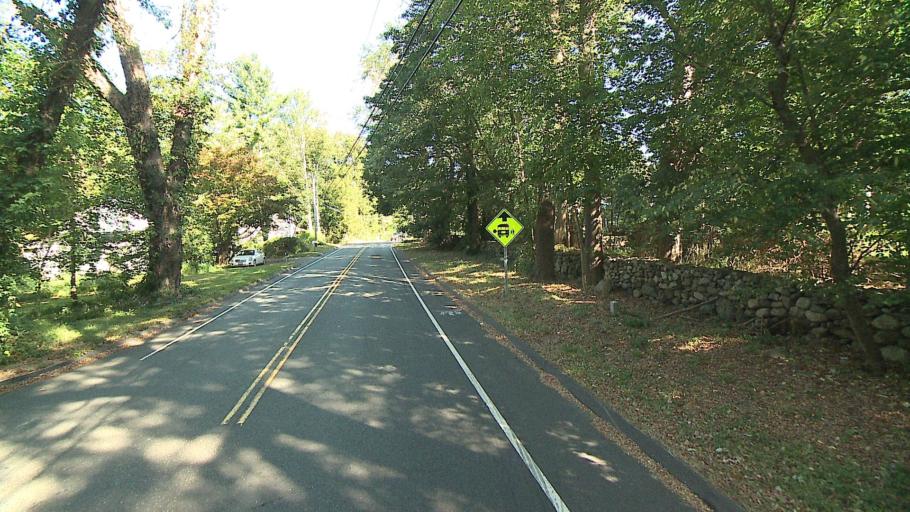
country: US
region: Connecticut
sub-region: Fairfield County
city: New Canaan
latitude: 41.1140
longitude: -73.4857
